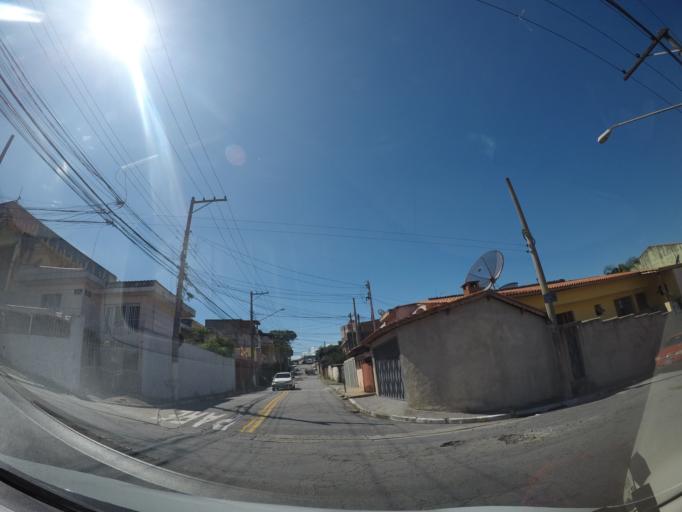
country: BR
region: Sao Paulo
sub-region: Guarulhos
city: Guarulhos
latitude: -23.4563
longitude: -46.5422
